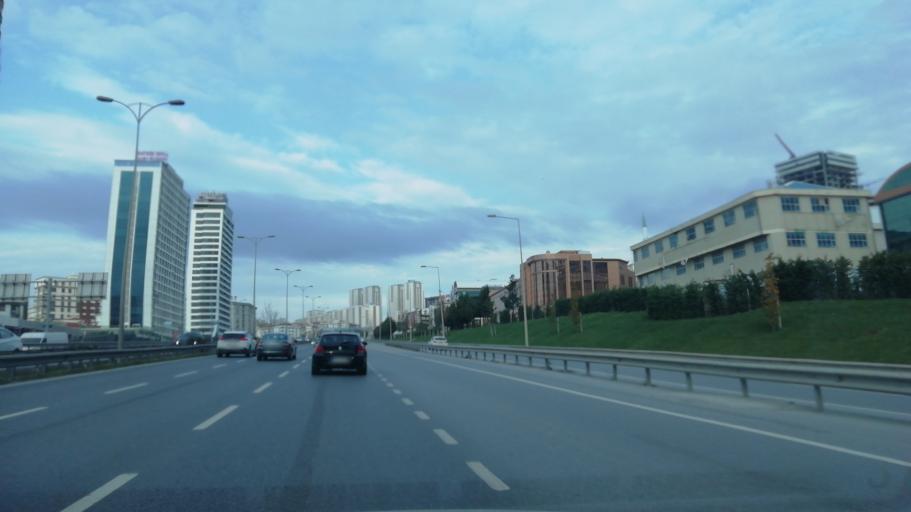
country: TR
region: Istanbul
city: Esenyurt
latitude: 41.0175
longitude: 28.6795
